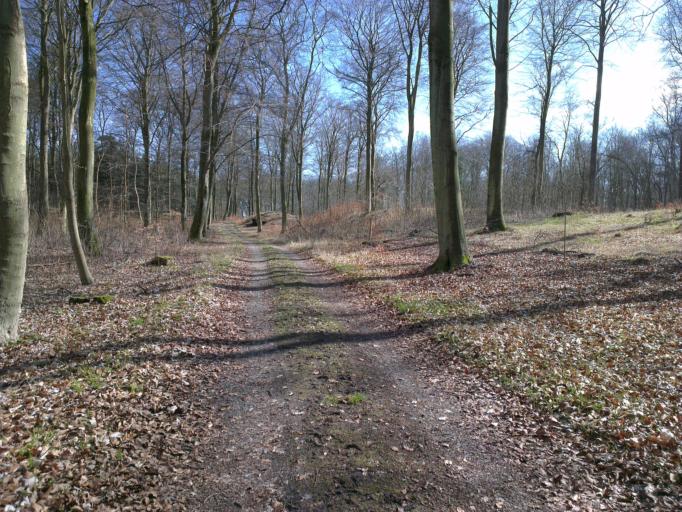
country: DK
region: Capital Region
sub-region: Frederikssund Kommune
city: Jaegerspris
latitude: 55.8847
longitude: 11.9934
